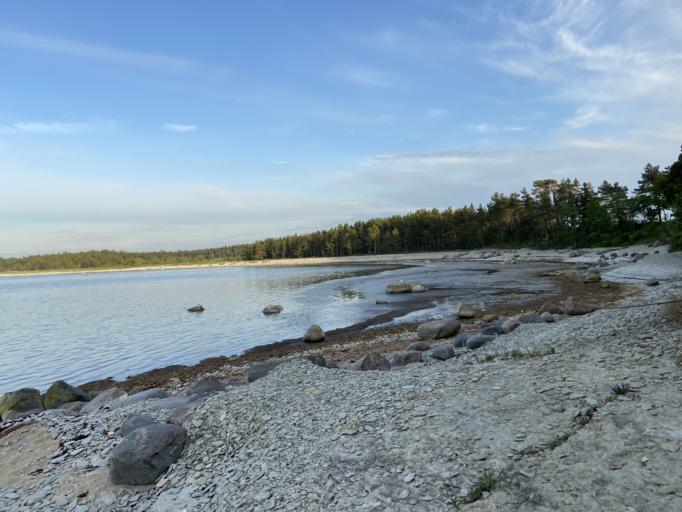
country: EE
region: Harju
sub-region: Paldiski linn
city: Paldiski
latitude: 59.2724
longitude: 23.7346
